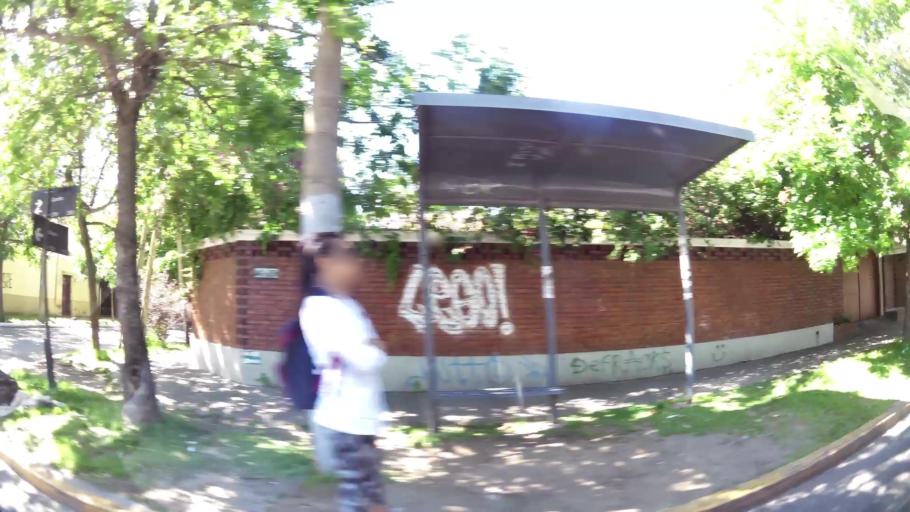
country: AR
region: Buenos Aires
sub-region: Partido de Quilmes
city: Quilmes
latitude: -34.7095
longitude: -58.2911
